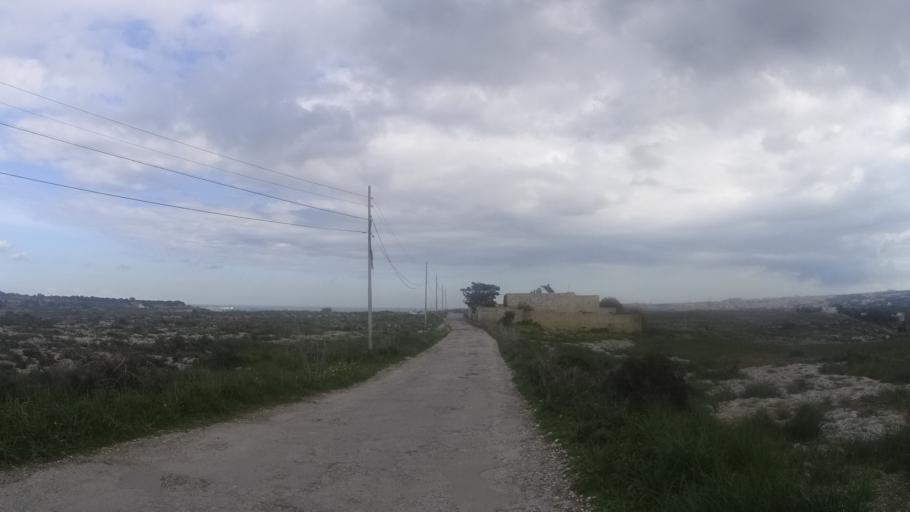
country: MT
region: L-Imgarr
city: Imgarr
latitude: 35.9008
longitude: 14.3742
